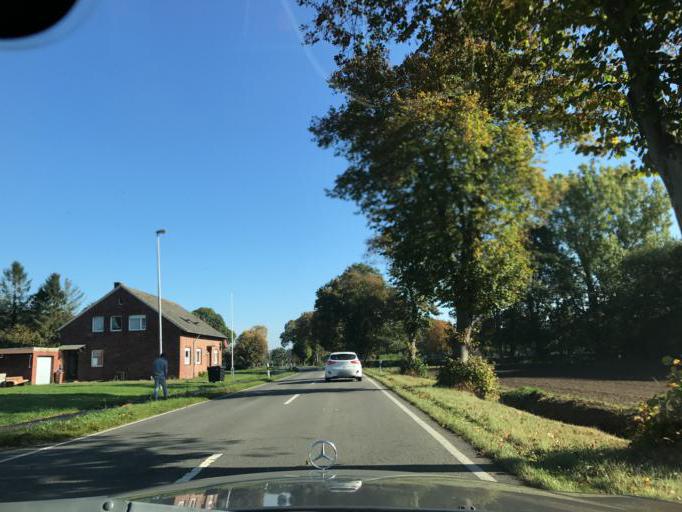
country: DE
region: Lower Saxony
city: Papenburg
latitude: 53.0888
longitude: 7.3668
